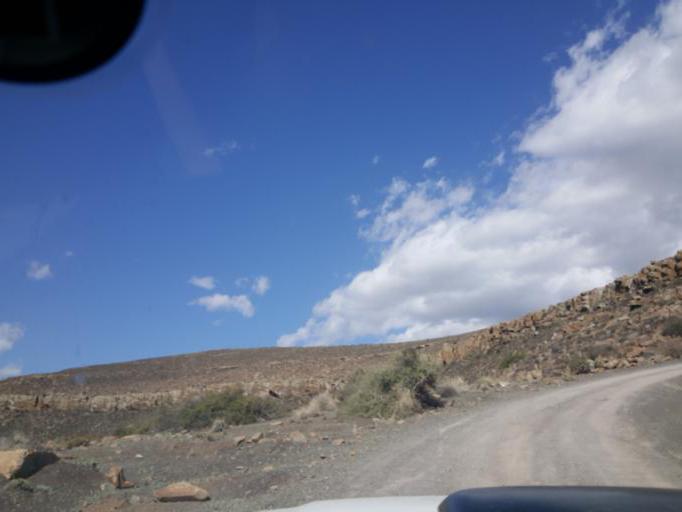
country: ZA
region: Western Cape
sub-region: Central Karoo District Municipality
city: Laingsburg
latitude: -32.4091
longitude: 20.3519
